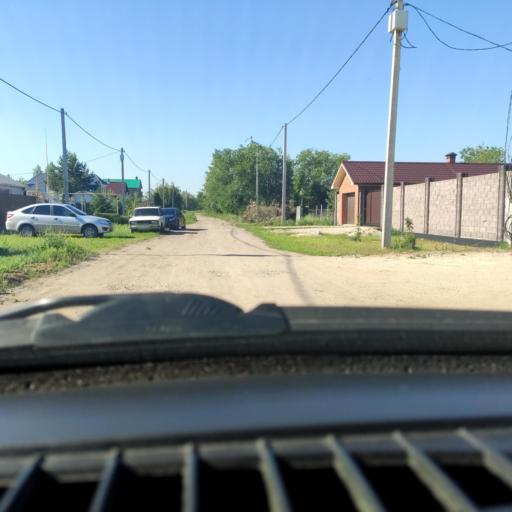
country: RU
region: Samara
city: Tol'yatti
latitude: 53.5595
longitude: 49.3779
